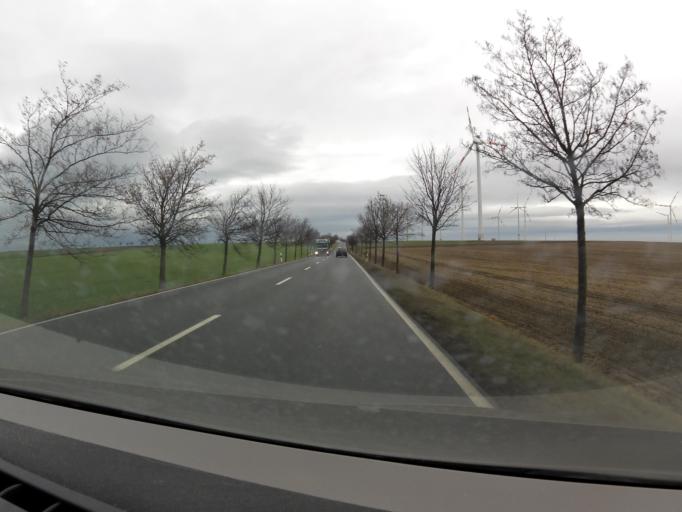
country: DE
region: Saxony-Anhalt
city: Aschersleben
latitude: 51.7054
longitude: 11.4573
